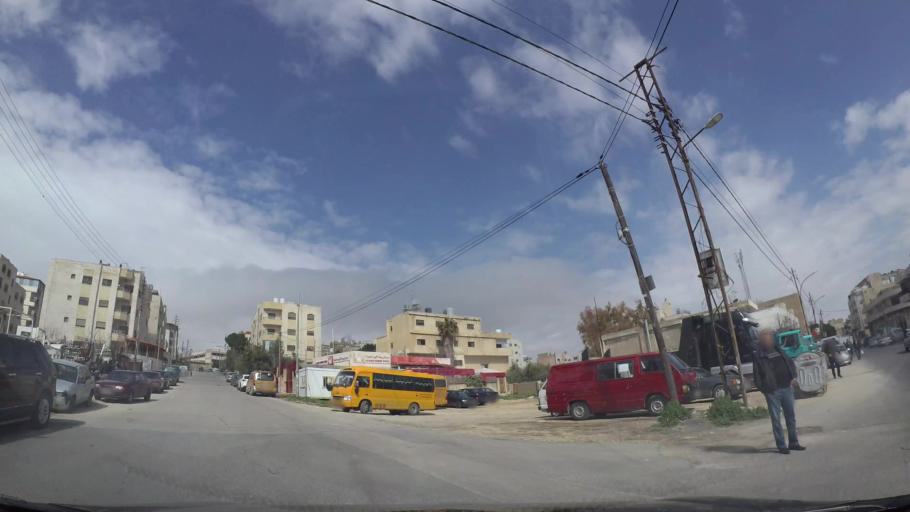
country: JO
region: Amman
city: Wadi as Sir
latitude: 31.9490
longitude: 35.8316
